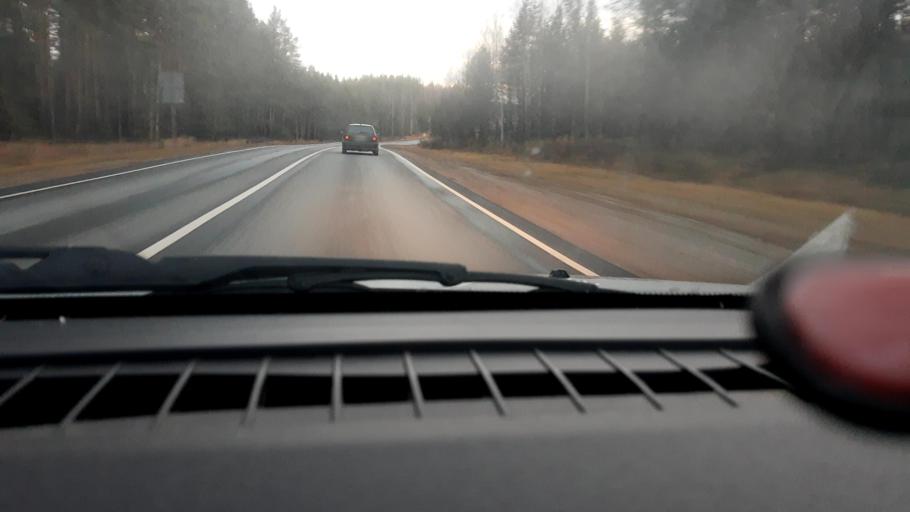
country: RU
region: Nizjnij Novgorod
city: Krasnyye Baki
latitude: 57.0233
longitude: 45.1170
